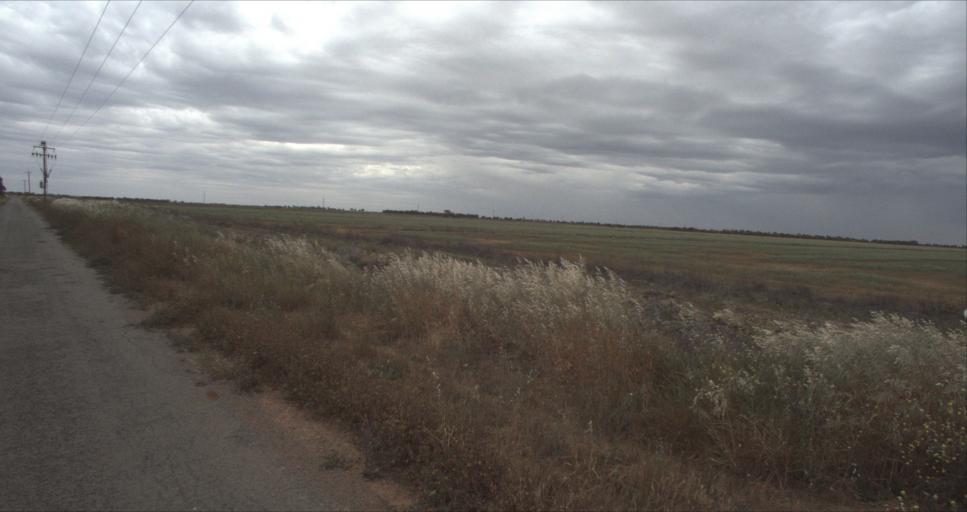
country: AU
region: New South Wales
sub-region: Leeton
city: Leeton
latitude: -34.4312
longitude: 146.3366
